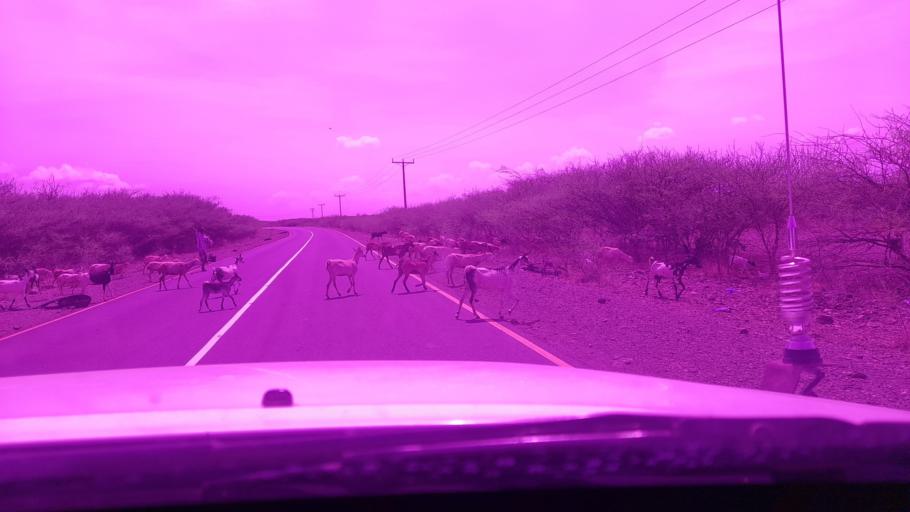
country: ET
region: Afar
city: Awash
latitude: 9.3524
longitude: 40.3002
